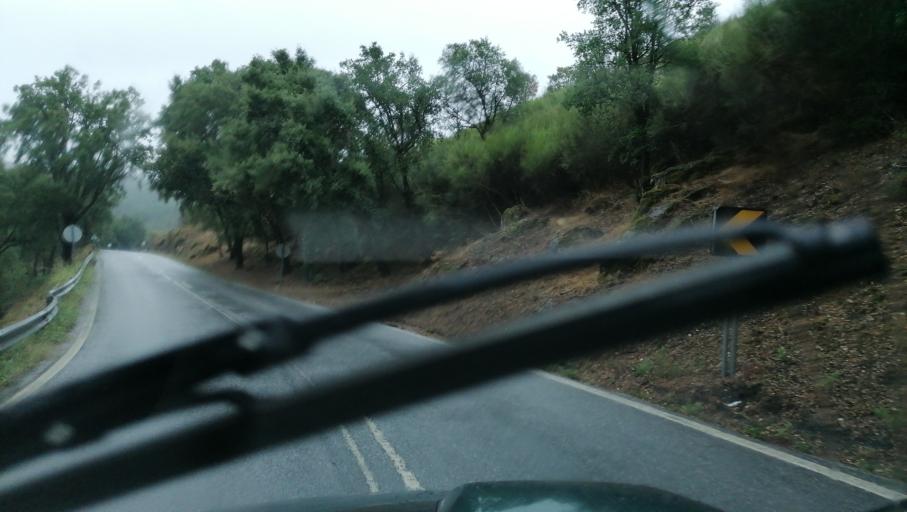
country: PT
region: Braga
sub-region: Cabeceiras de Basto
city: Cabeceiras de Basto
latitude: 41.4912
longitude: -7.9378
